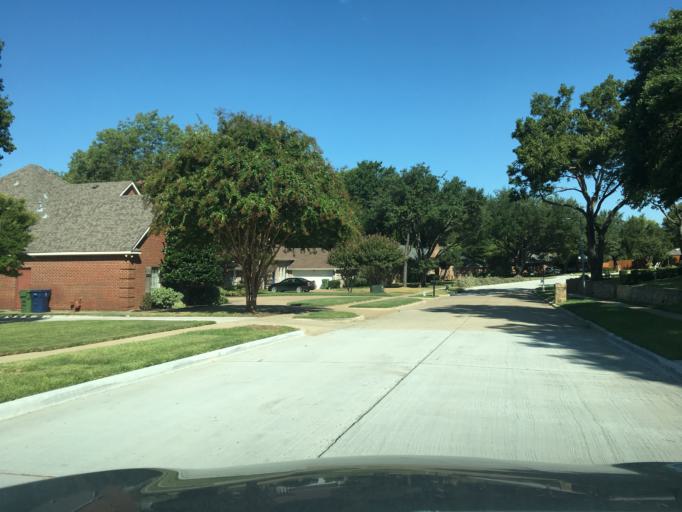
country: US
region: Texas
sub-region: Dallas County
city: Sachse
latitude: 32.9669
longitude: -96.6109
